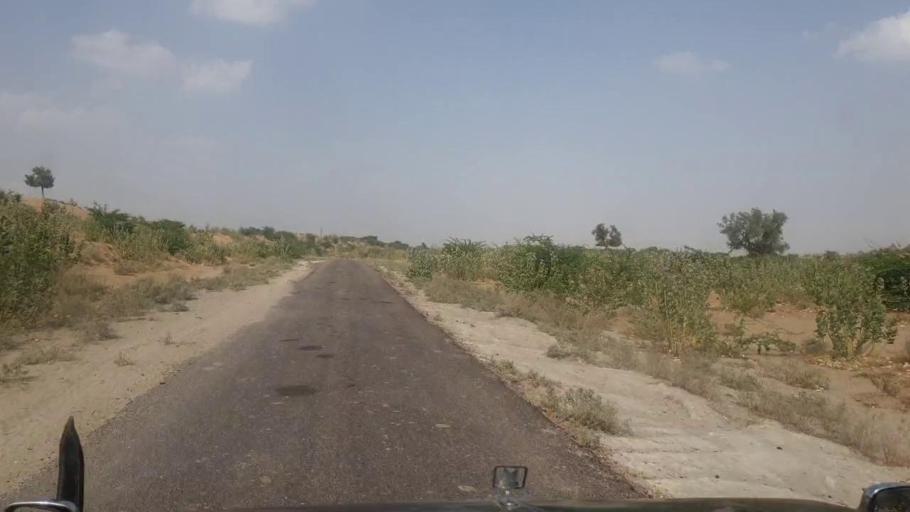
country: PK
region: Sindh
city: Islamkot
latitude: 25.2107
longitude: 70.2843
